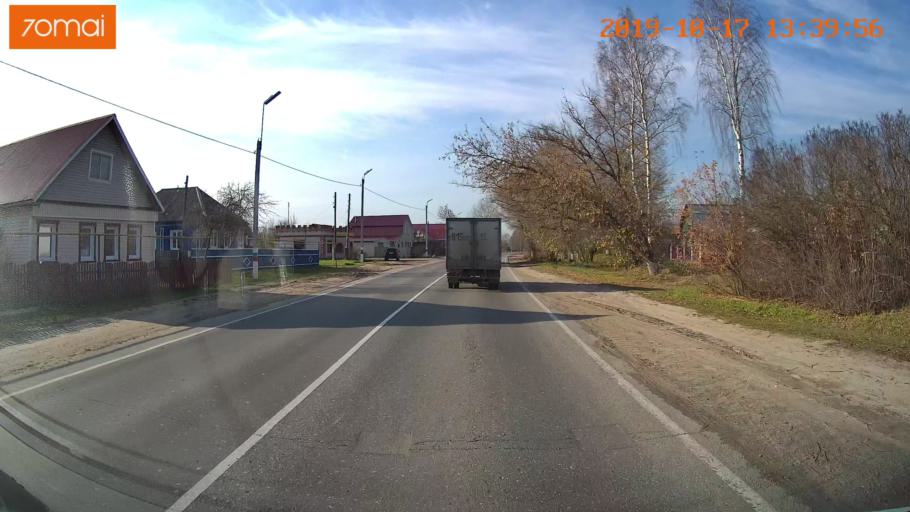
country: RU
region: Rjazan
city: Tuma
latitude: 55.1466
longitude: 40.5792
